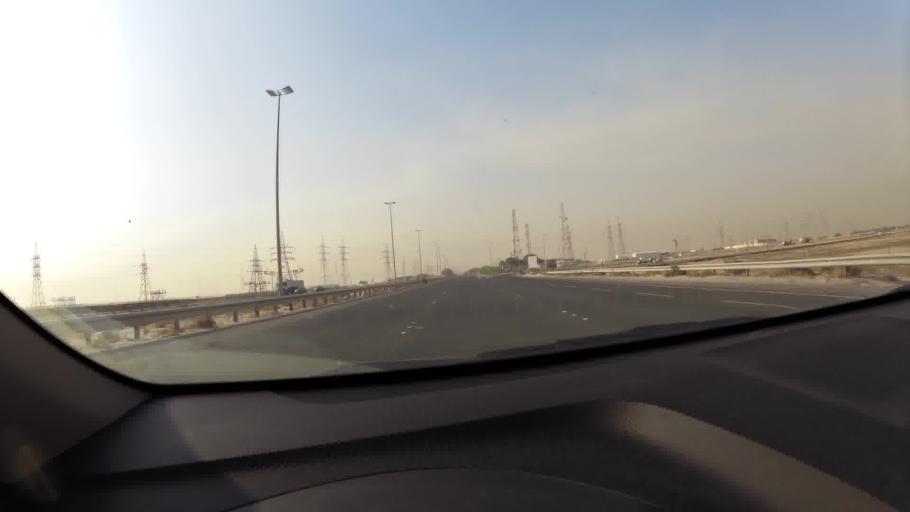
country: SA
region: Eastern Province
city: Al Khafji
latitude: 28.7376
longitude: 48.2846
